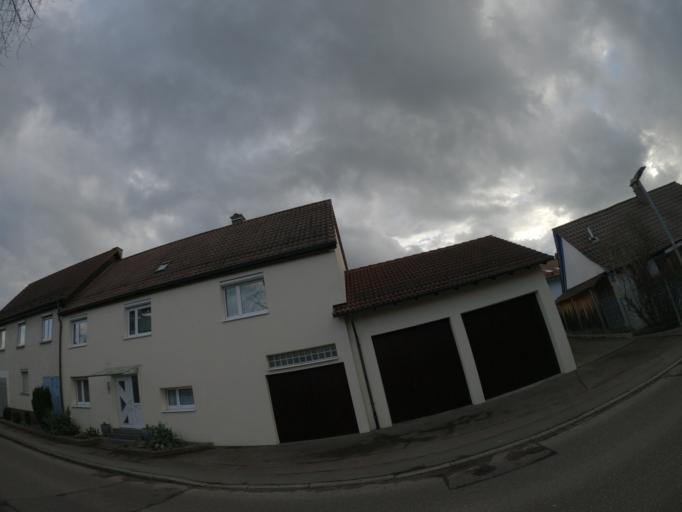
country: DE
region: Baden-Wuerttemberg
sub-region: Regierungsbezirk Stuttgart
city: Boll
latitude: 48.6676
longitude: 9.6167
